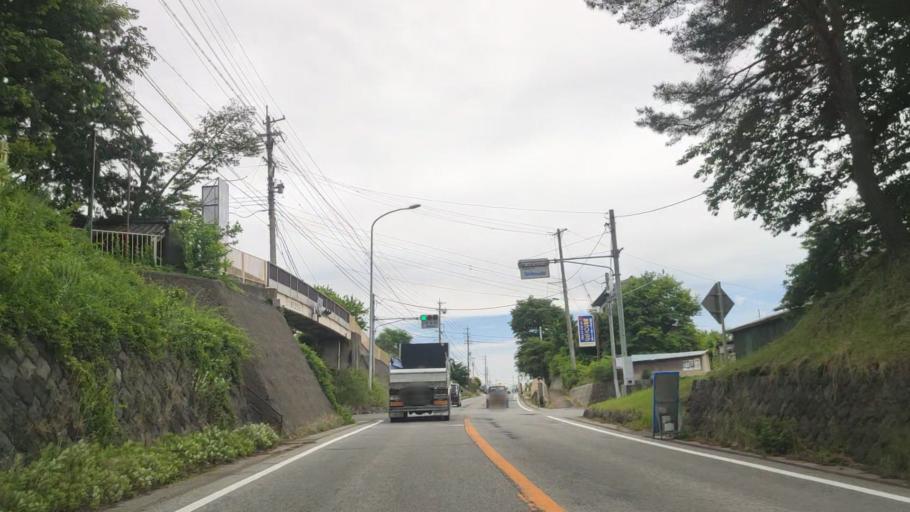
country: JP
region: Nagano
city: Komoro
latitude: 36.3427
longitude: 138.3868
